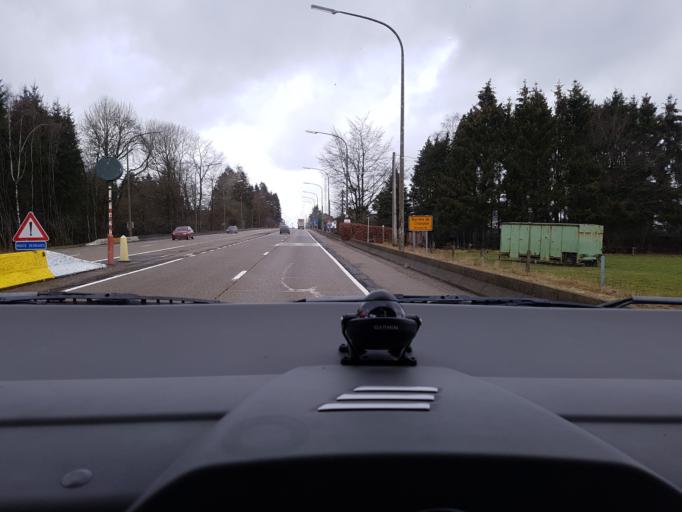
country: BE
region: Wallonia
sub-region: Province du Luxembourg
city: Tenneville
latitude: 50.1015
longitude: 5.4794
